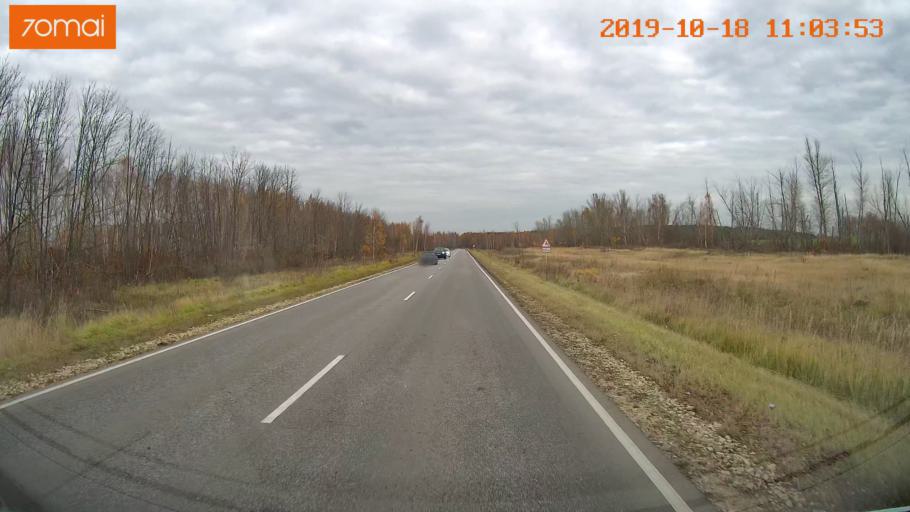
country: RU
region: Tula
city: Yepifan'
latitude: 53.8865
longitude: 38.5497
